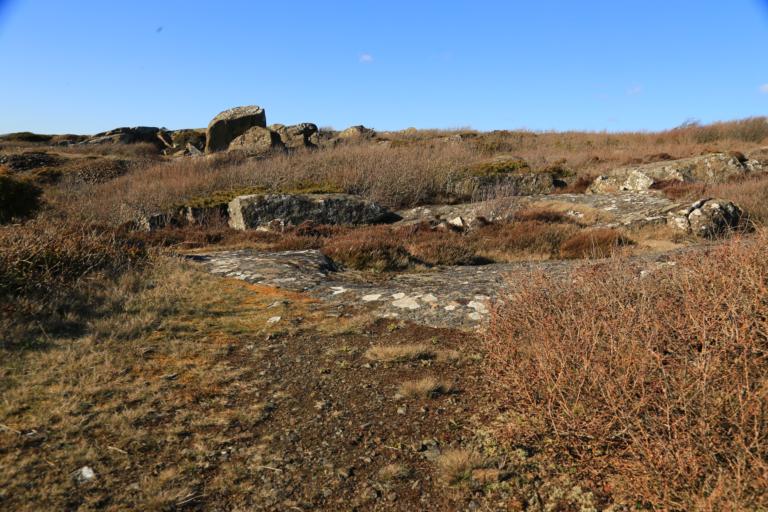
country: SE
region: Halland
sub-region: Varbergs Kommun
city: Varberg
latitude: 57.0928
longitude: 12.2412
